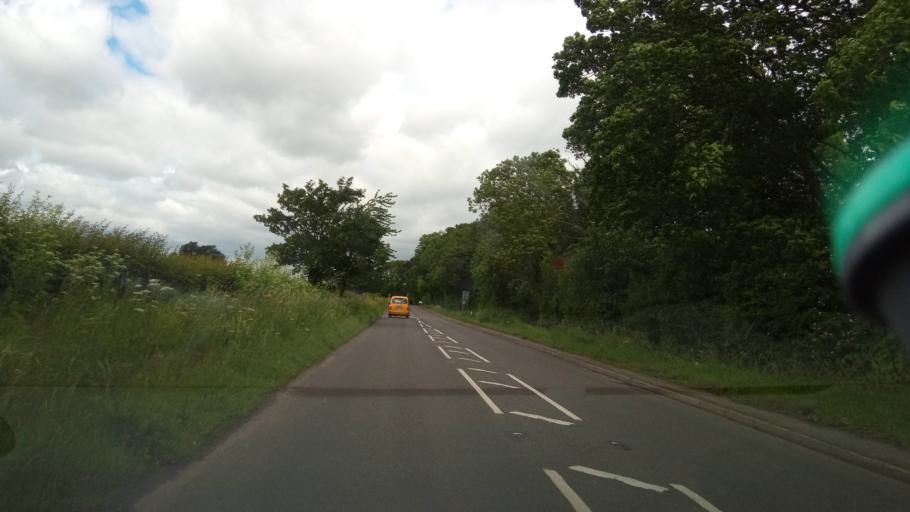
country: GB
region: England
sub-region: Derbyshire
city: Etwall
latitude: 52.8597
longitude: -1.6031
